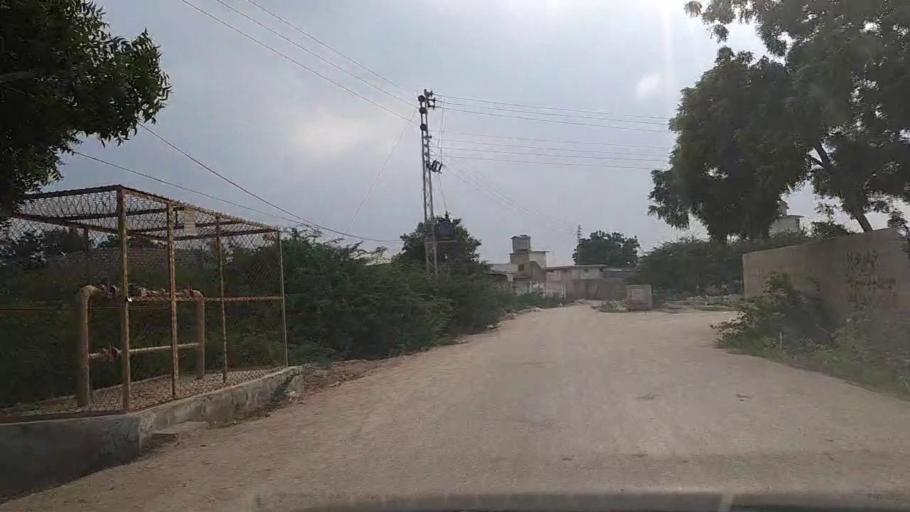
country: PK
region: Sindh
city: Thatta
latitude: 24.8449
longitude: 67.7762
